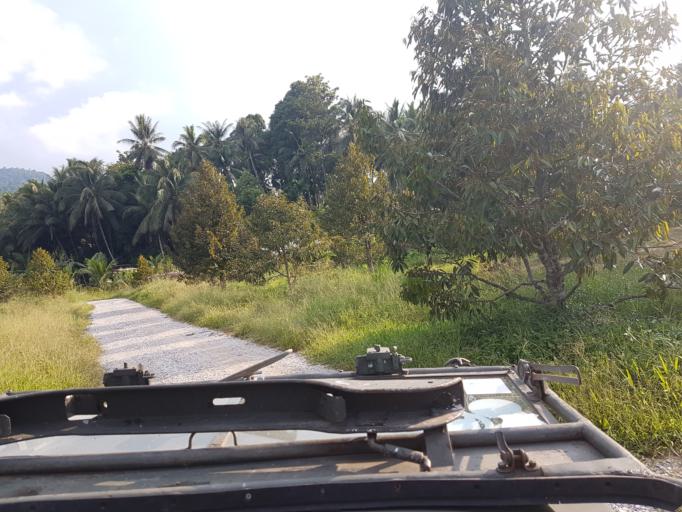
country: TH
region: Pattani
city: Khok Pho
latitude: 6.6647
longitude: 101.0907
